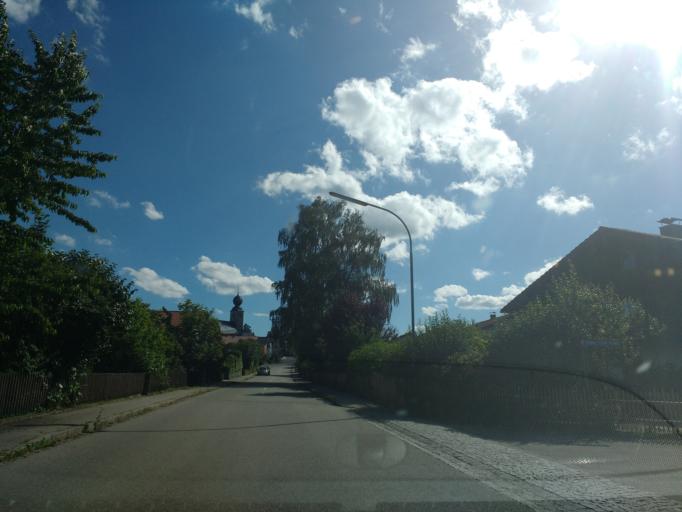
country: DE
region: Bavaria
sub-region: Upper Bavaria
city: Engelsberg
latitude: 48.1191
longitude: 12.5455
